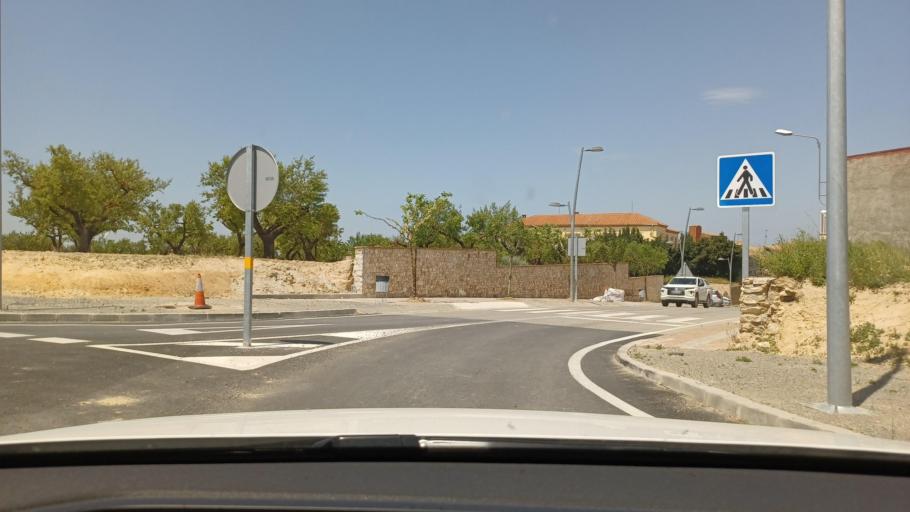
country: ES
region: Catalonia
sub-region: Provincia de Tarragona
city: Vilalba dels Arcs
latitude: 41.1172
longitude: 0.4091
